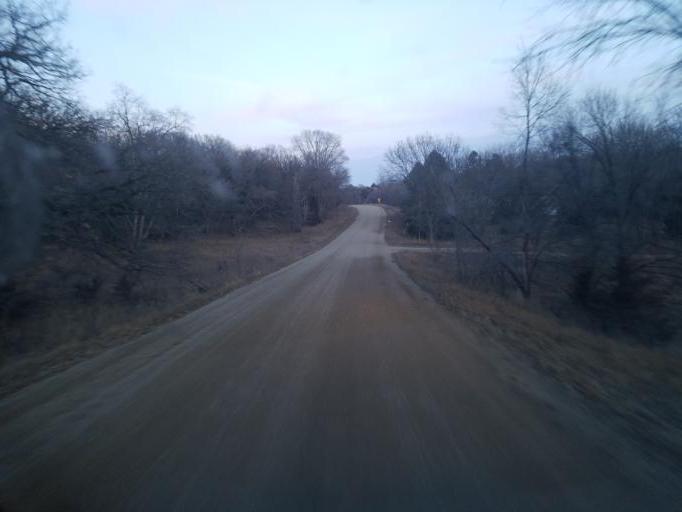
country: US
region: Nebraska
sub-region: Knox County
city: Center
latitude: 42.6107
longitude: -97.8625
